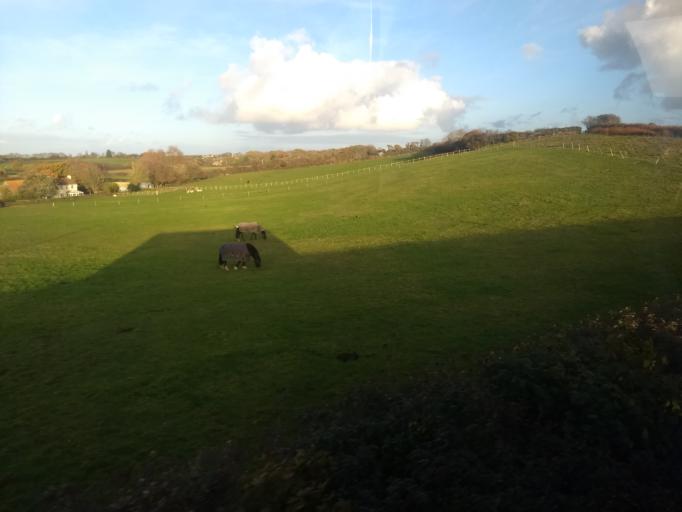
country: GB
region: England
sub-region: Isle of Wight
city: Shalfleet
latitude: 50.6809
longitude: -1.4078
